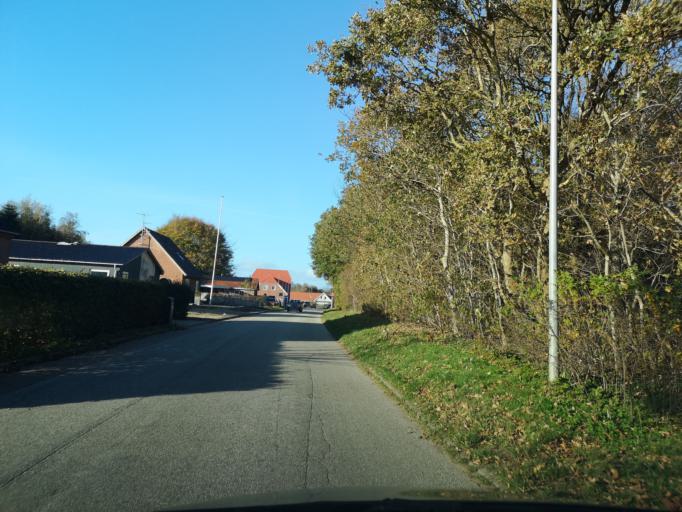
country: DK
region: Central Jutland
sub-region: Ringkobing-Skjern Kommune
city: Tarm
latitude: 55.8206
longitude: 8.4108
